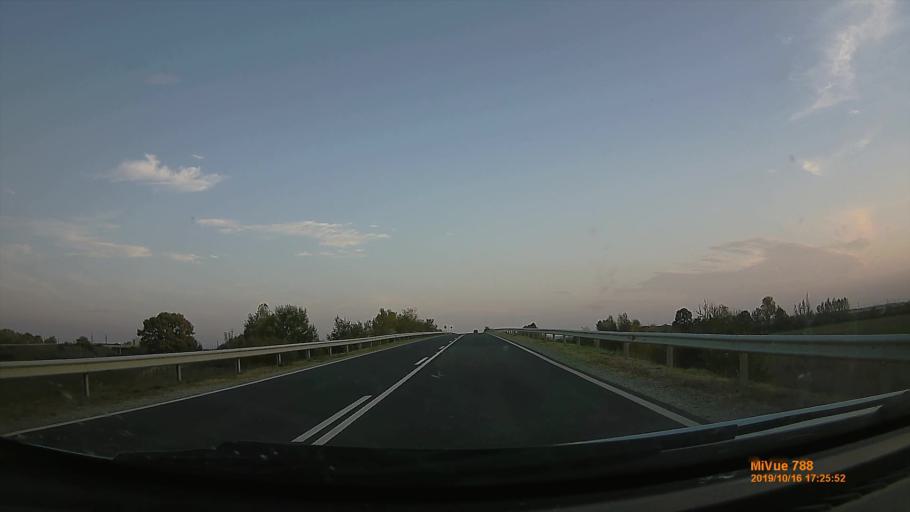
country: HU
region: Heves
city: Fuzesabony
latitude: 47.7514
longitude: 20.3972
